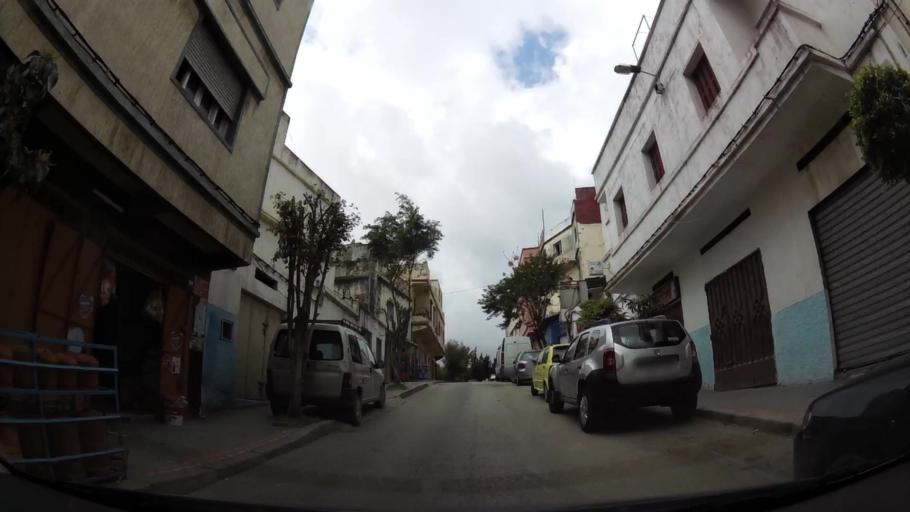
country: MA
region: Tanger-Tetouan
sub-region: Tanger-Assilah
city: Tangier
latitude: 35.7679
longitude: -5.8223
